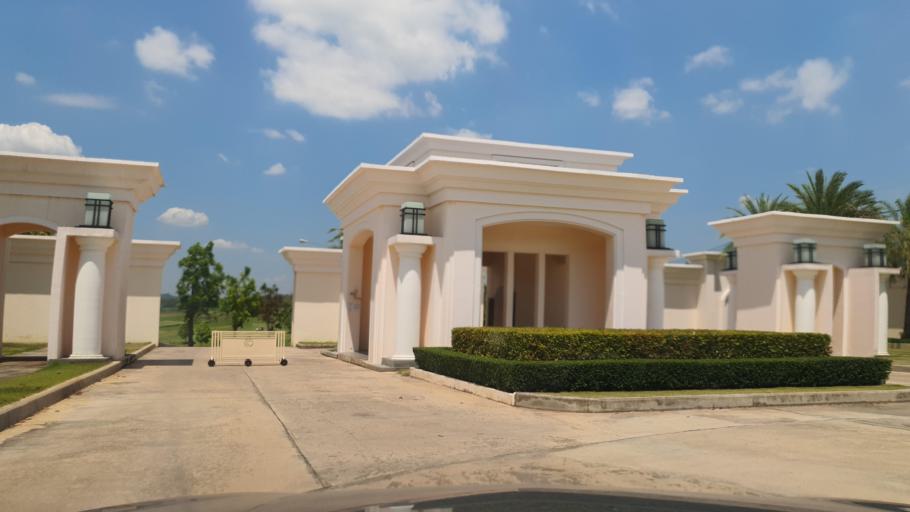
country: TH
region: Rayong
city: Ban Chang
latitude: 12.7682
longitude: 100.9610
